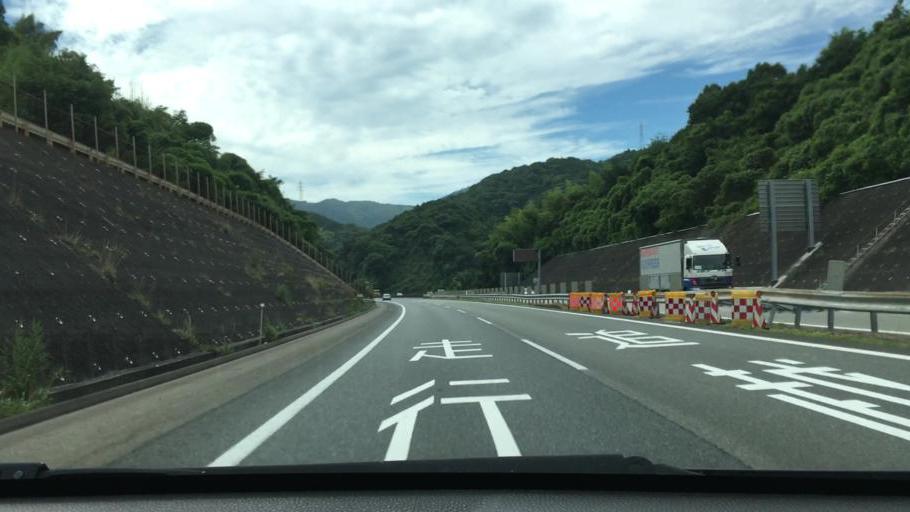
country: JP
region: Yamaguchi
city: Hofu
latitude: 34.0715
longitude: 131.6815
